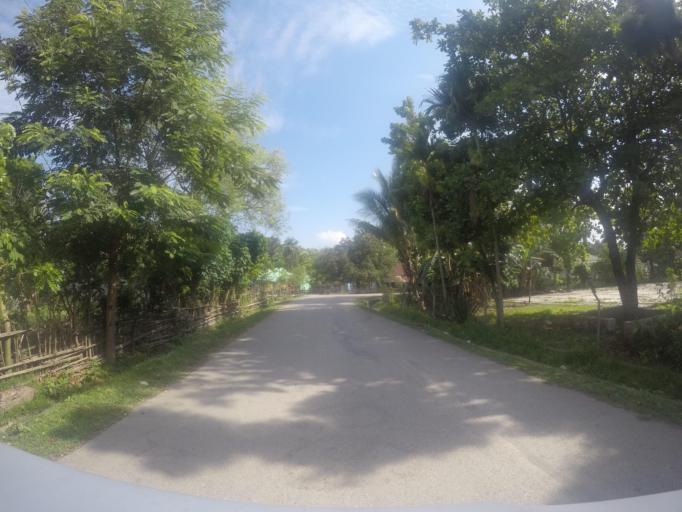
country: TL
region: Viqueque
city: Viqueque
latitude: -8.8553
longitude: 126.3622
